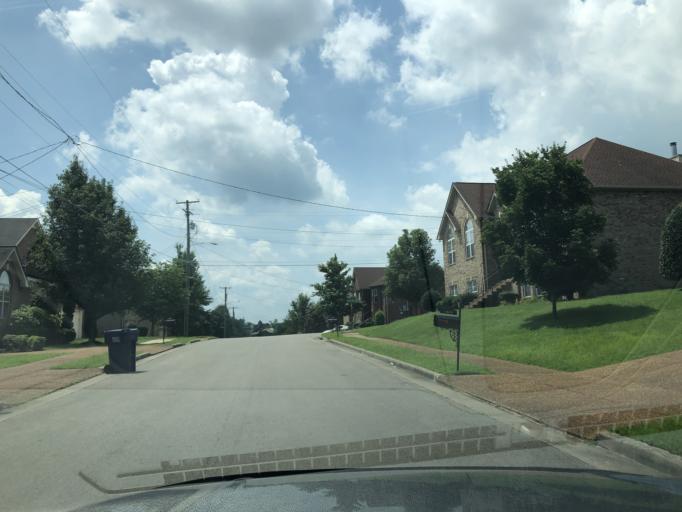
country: US
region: Tennessee
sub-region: Williamson County
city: Nolensville
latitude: 36.0168
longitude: -86.6939
